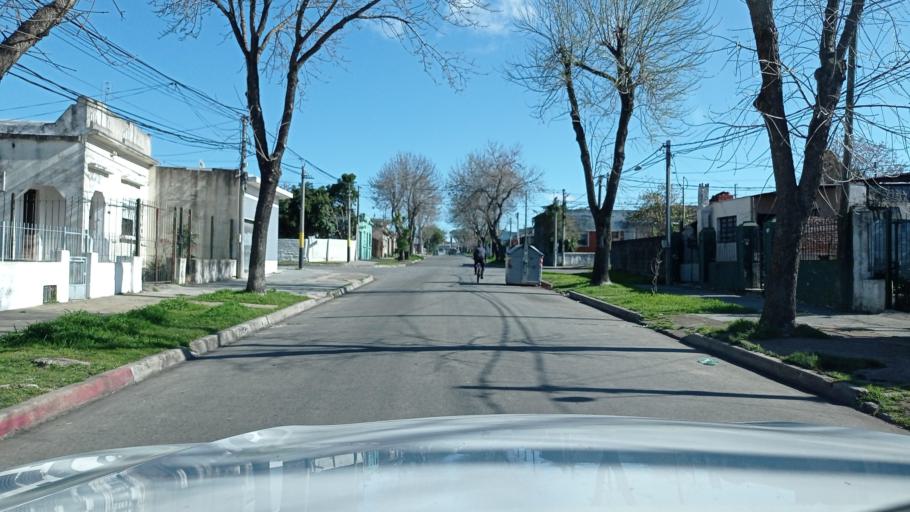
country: UY
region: Montevideo
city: Montevideo
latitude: -34.8528
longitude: -56.1590
